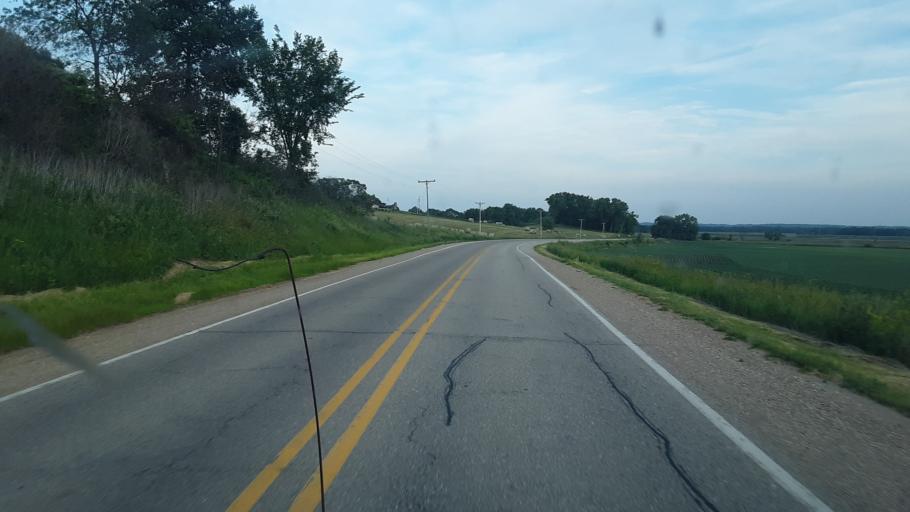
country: US
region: Iowa
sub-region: Tama County
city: Tama
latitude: 41.9560
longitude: -92.4246
